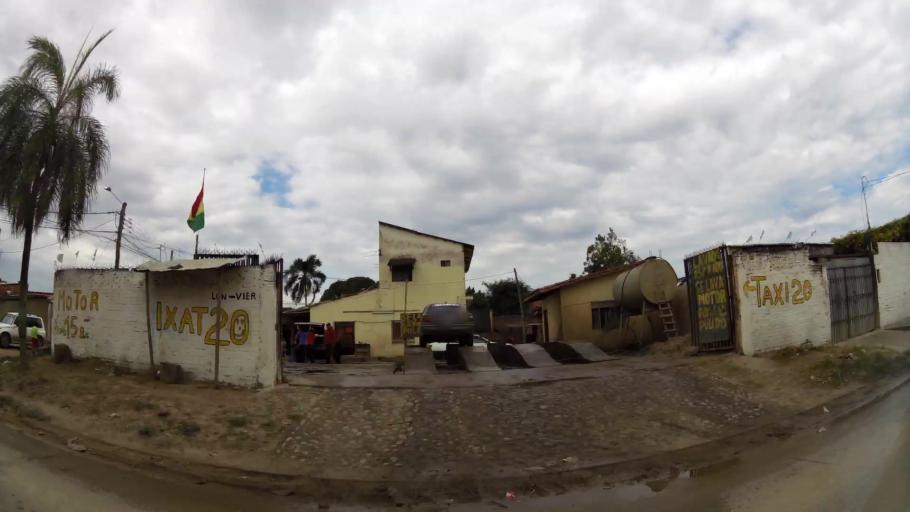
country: BO
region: Santa Cruz
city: Santa Cruz de la Sierra
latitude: -17.7410
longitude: -63.1823
